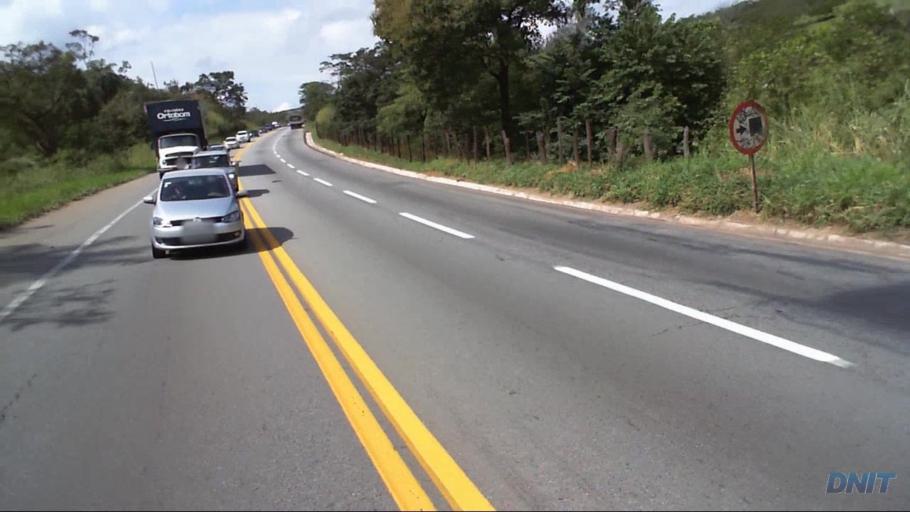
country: BR
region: Minas Gerais
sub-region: Santa Luzia
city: Santa Luzia
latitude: -19.8098
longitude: -43.7925
